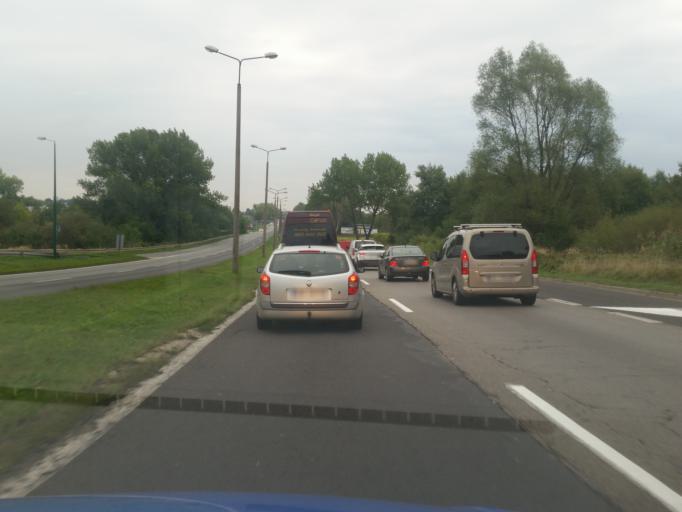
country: PL
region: Silesian Voivodeship
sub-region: Powiat bedzinski
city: Bedzin
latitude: 50.3027
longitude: 19.1750
